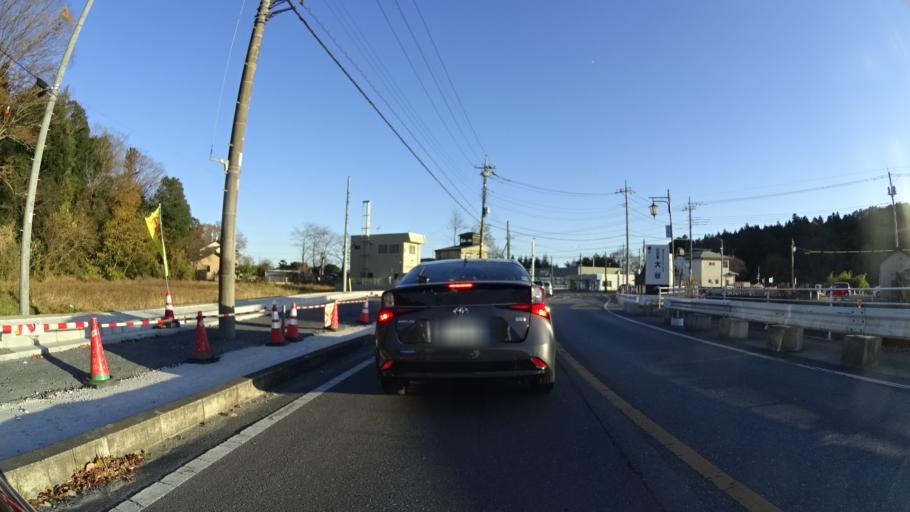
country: JP
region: Tochigi
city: Utsunomiya-shi
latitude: 36.5918
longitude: 139.8224
